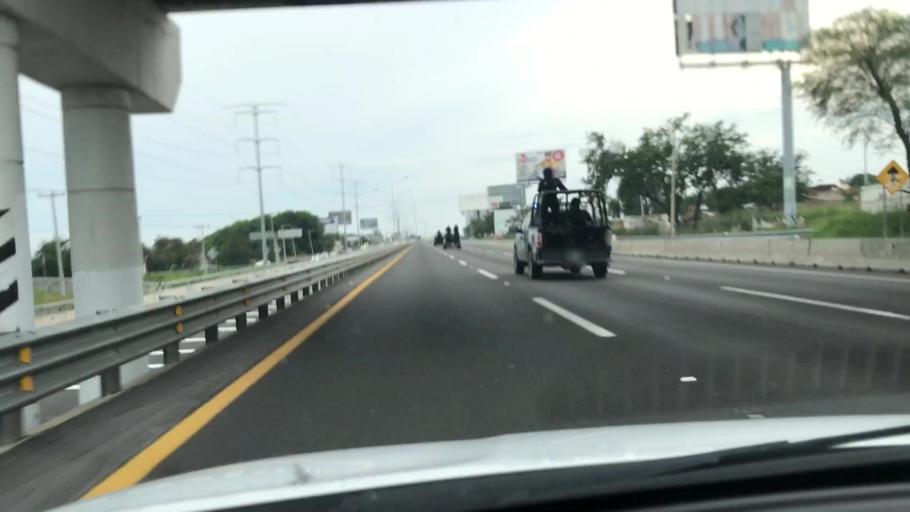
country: MX
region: Jalisco
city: Tonala
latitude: 20.6154
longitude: -103.2417
